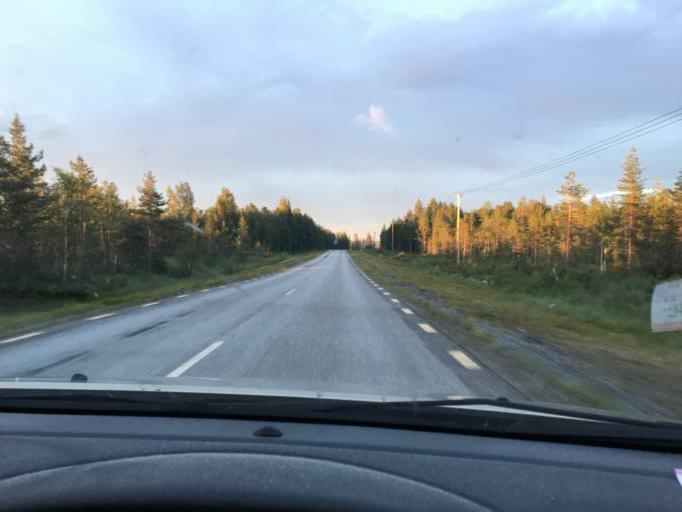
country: SE
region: Norrbotten
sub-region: Kalix Kommun
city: Toere
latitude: 66.0646
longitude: 22.6480
